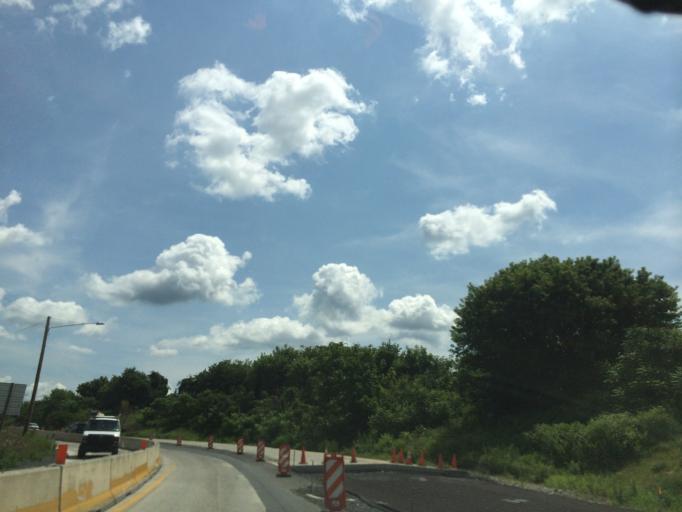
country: US
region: Pennsylvania
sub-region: Northampton County
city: Hellertown
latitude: 40.5940
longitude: -75.3372
